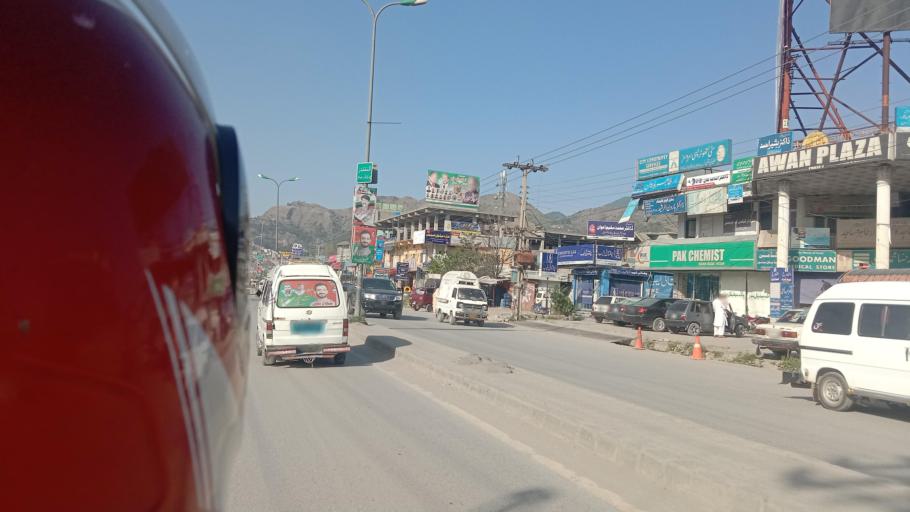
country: PK
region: Khyber Pakhtunkhwa
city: Abbottabad
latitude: 34.1963
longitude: 73.2364
